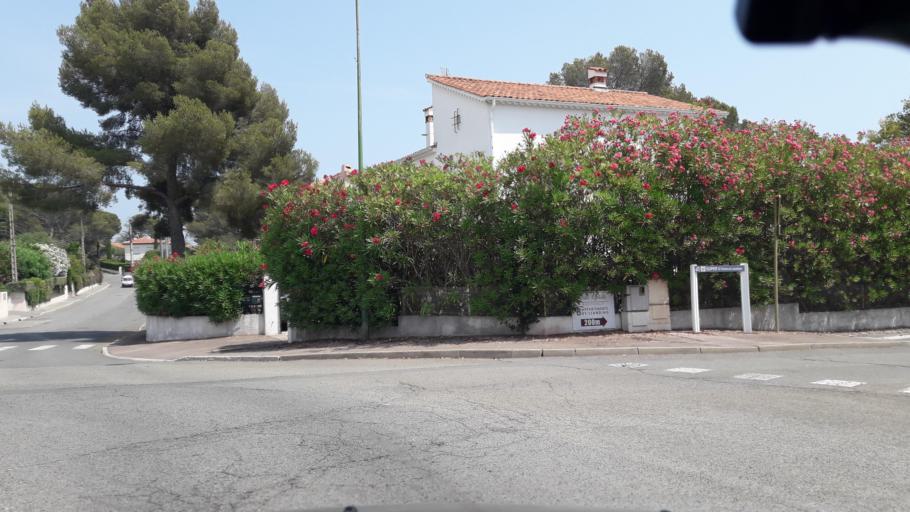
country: FR
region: Provence-Alpes-Cote d'Azur
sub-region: Departement du Var
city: Saint-Raphael
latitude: 43.4193
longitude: 6.7955
